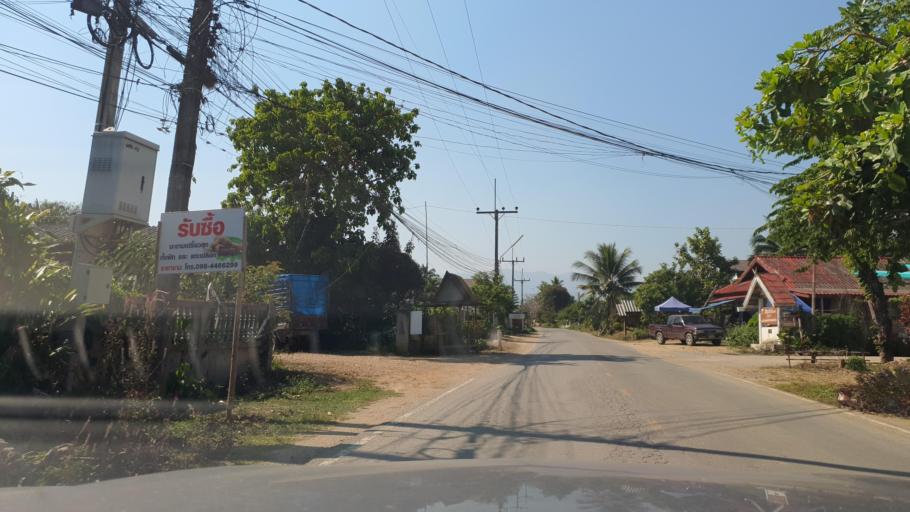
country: TH
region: Chiang Rai
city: Mae Lao
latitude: 19.7634
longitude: 99.7190
